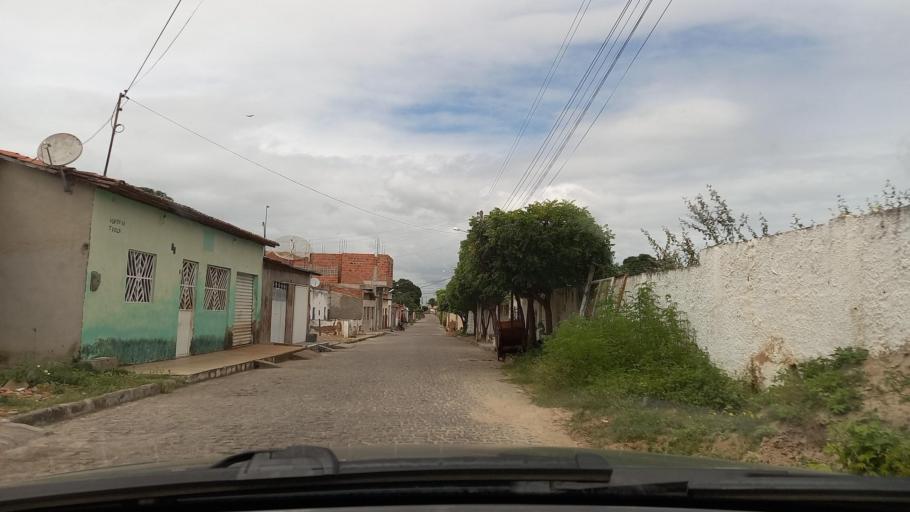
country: BR
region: Sergipe
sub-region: Caninde De Sao Francisco
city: Caninde de Sao Francisco
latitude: -9.6077
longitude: -37.7589
